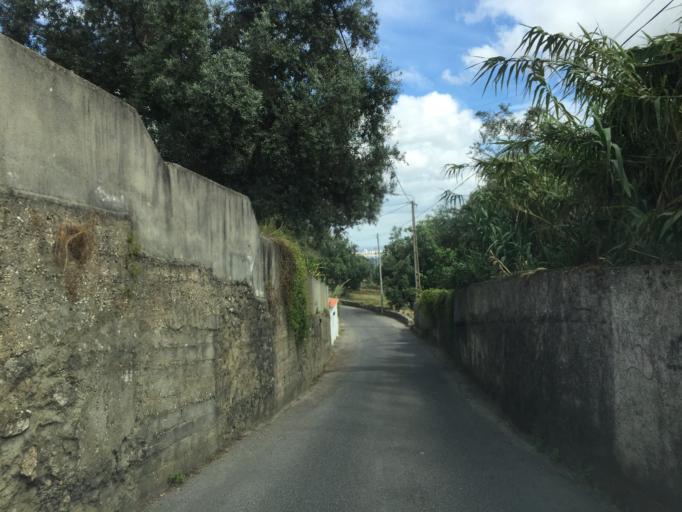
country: PT
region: Lisbon
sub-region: Odivelas
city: Famoes
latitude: 38.7899
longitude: -9.2293
